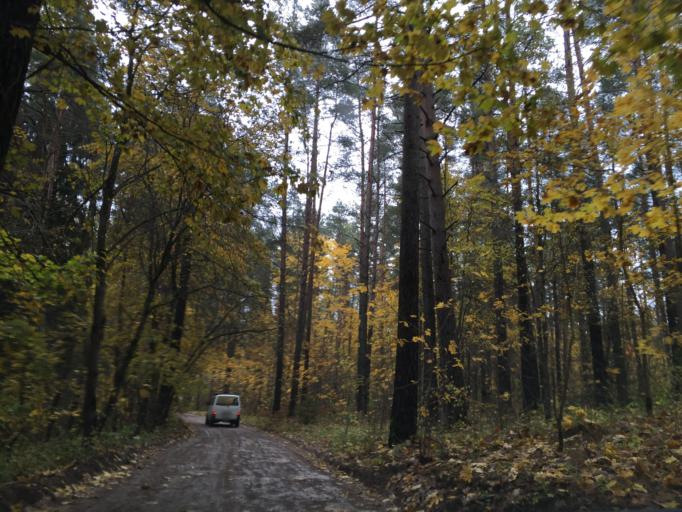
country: LV
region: Ogre
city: Ogre
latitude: 56.8001
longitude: 24.6463
